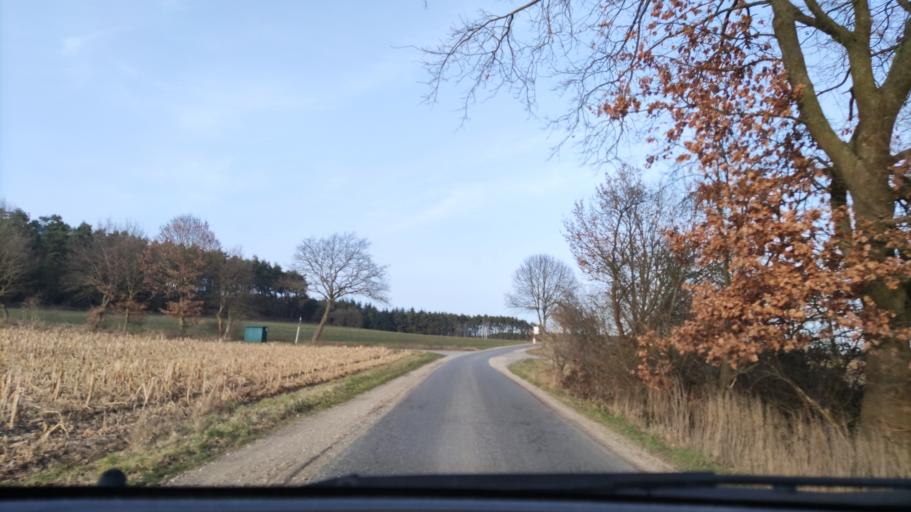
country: DE
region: Lower Saxony
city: Dahlenburg
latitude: 53.1966
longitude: 10.6973
